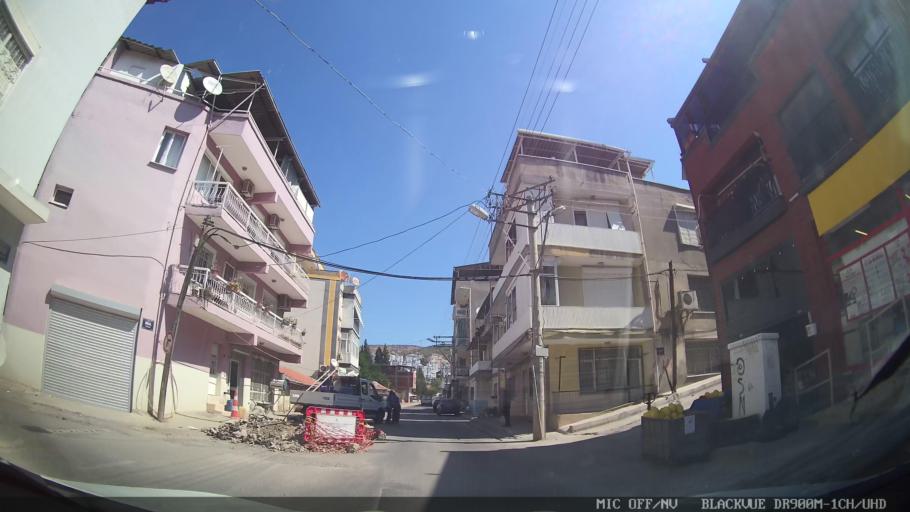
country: TR
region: Izmir
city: Karsiyaka
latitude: 38.4963
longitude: 27.0672
